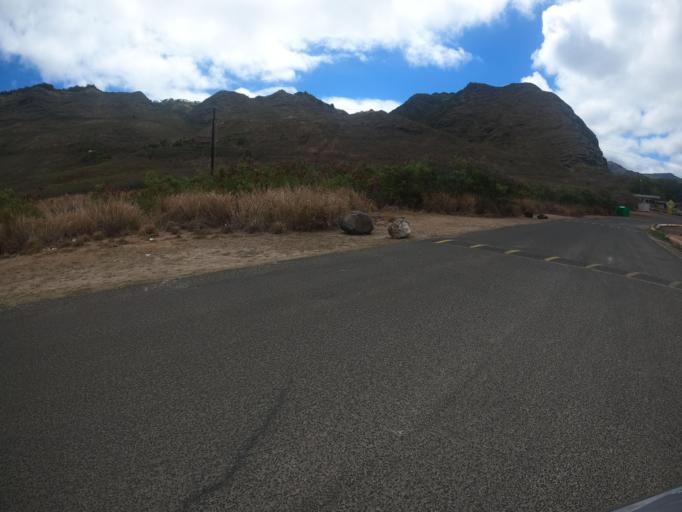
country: US
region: Hawaii
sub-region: Honolulu County
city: Makaha Valley
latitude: 21.5478
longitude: -158.2407
